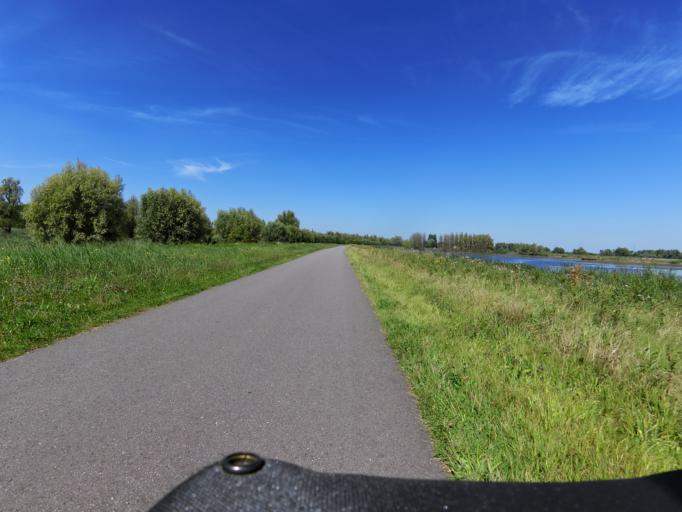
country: NL
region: South Holland
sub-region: Gemeente Sliedrecht
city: Sliedrecht
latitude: 51.7706
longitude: 4.7566
